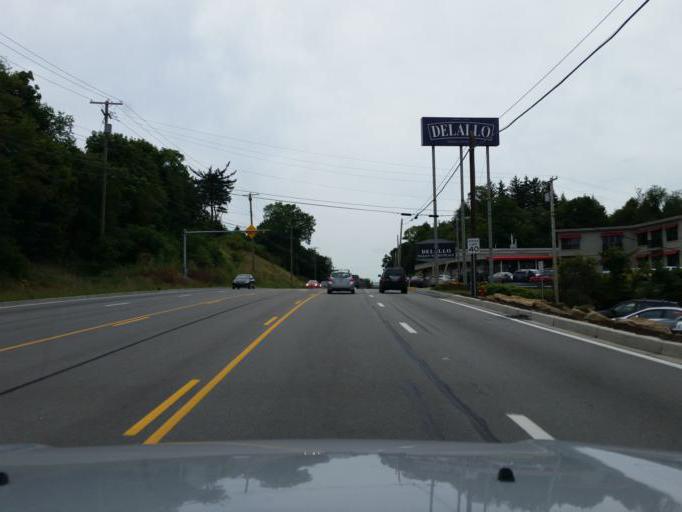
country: US
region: Pennsylvania
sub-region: Westmoreland County
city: Jeannette
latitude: 40.3110
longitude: -79.6083
